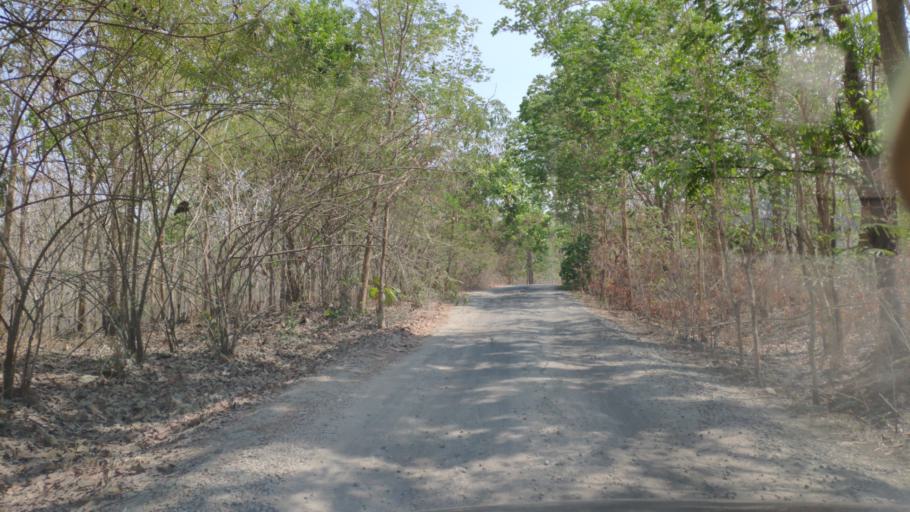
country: ID
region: Central Java
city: Gaplokan
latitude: -6.8819
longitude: 111.2666
